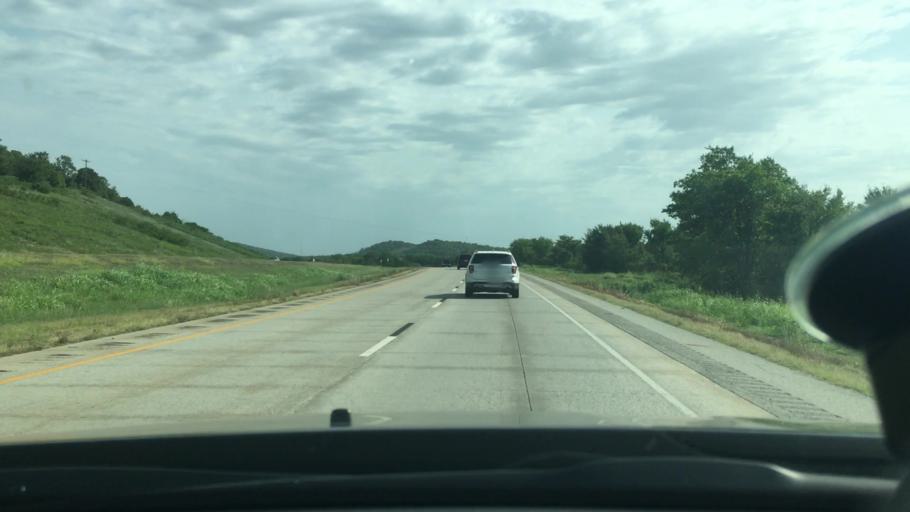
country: US
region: Oklahoma
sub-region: Atoka County
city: Atoka
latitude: 34.4355
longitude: -96.0769
